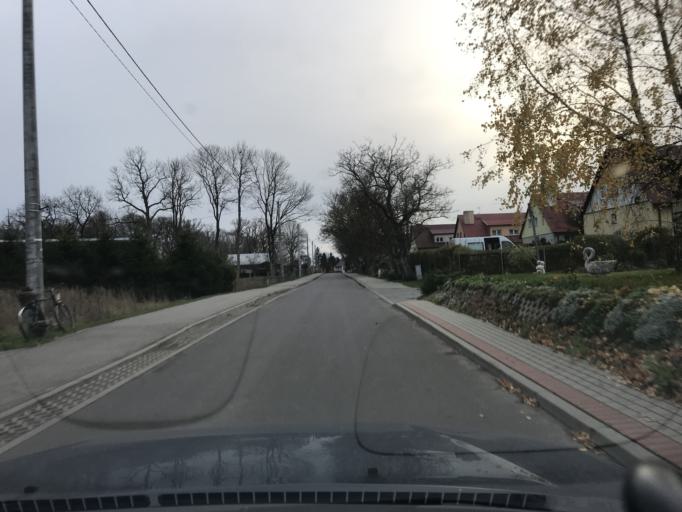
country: PL
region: Pomeranian Voivodeship
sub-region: Powiat slupski
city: Kobylnica
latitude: 54.4555
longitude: 16.8815
